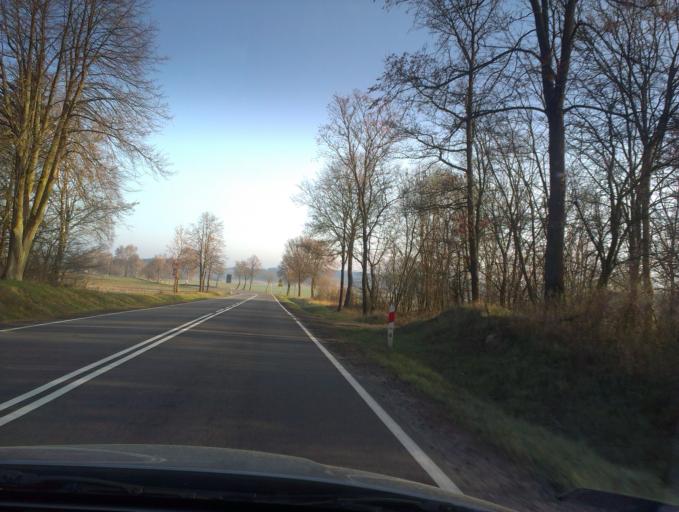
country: PL
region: West Pomeranian Voivodeship
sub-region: Powiat szczecinecki
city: Szczecinek
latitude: 53.7517
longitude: 16.6535
